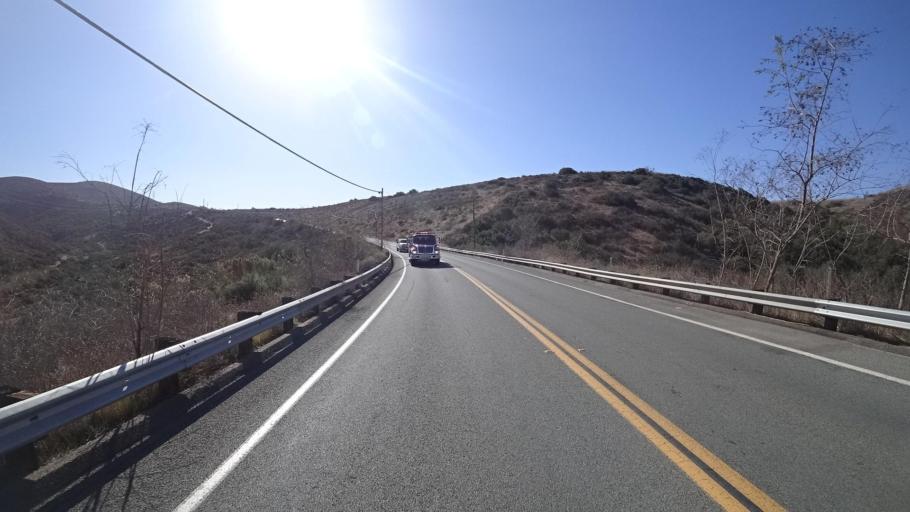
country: MX
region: Baja California
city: Tijuana
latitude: 32.5861
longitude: -116.9262
